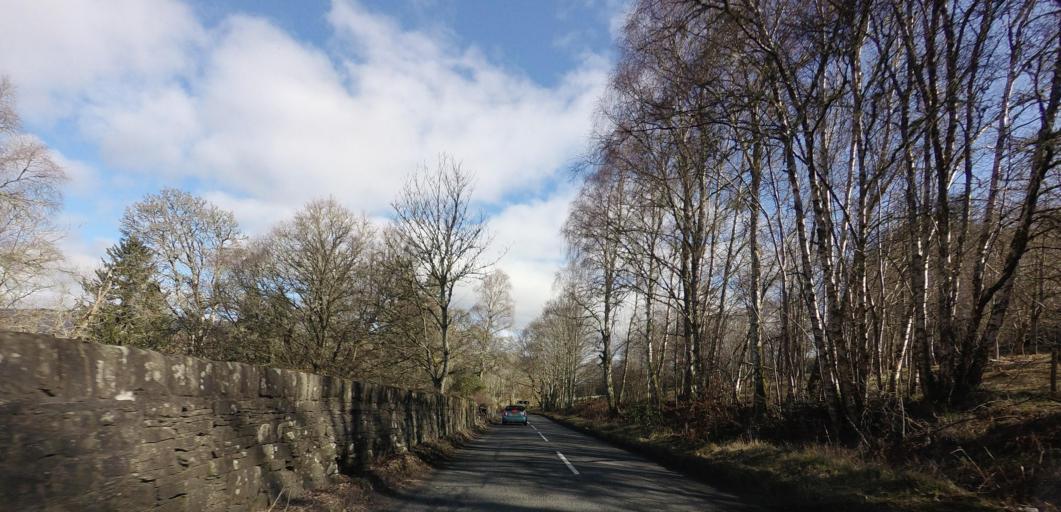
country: GB
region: Scotland
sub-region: Perth and Kinross
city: Aberfeldy
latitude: 56.5958
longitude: -3.9669
